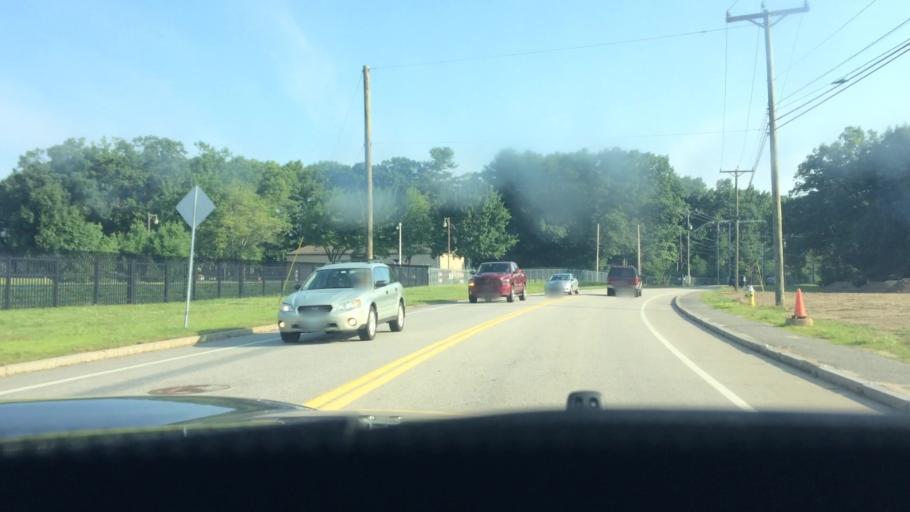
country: US
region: Maine
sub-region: York County
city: South Eliot
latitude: 43.0884
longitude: -70.8140
